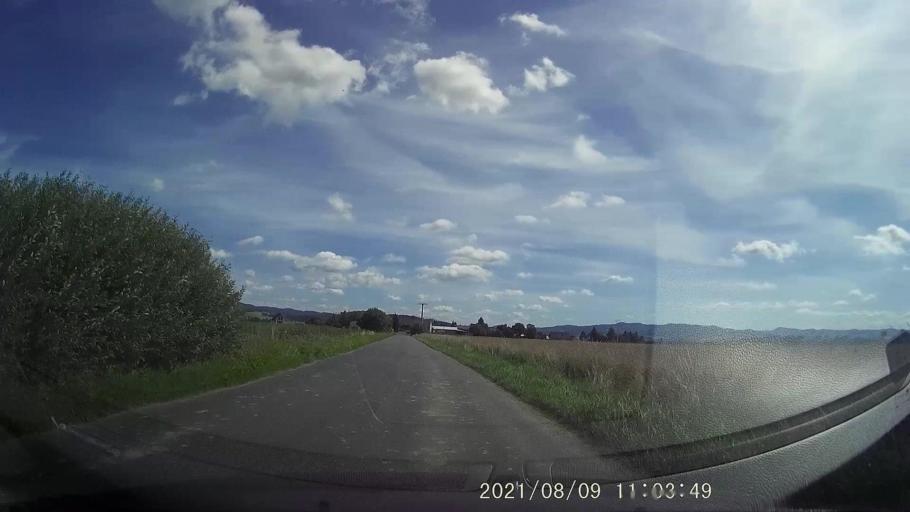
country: PL
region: Lower Silesian Voivodeship
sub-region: Powiat klodzki
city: Bozkow
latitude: 50.4623
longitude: 16.5652
